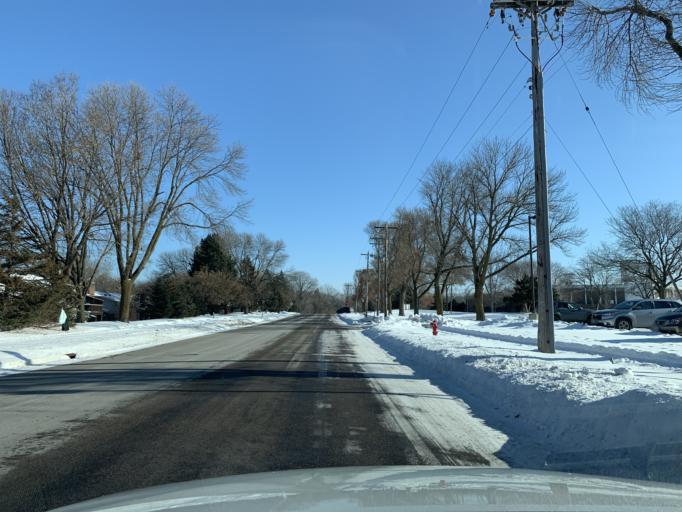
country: US
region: Minnesota
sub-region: Hennepin County
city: Edina
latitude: 44.8332
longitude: -93.3600
